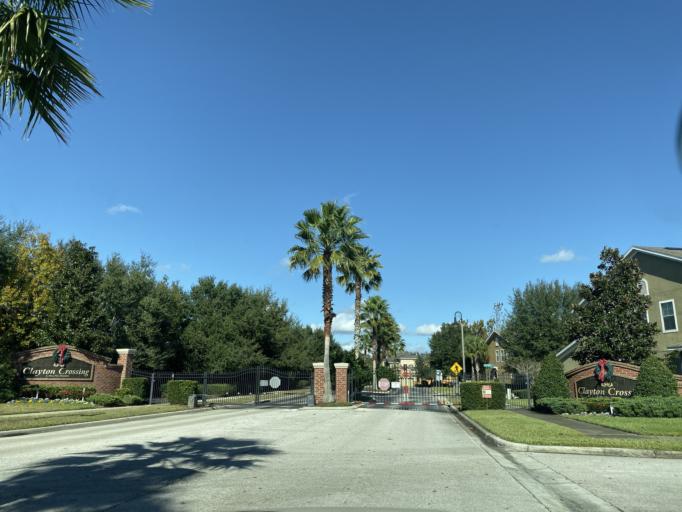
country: US
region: Florida
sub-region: Seminole County
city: Goldenrod
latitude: 28.6211
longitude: -81.2617
